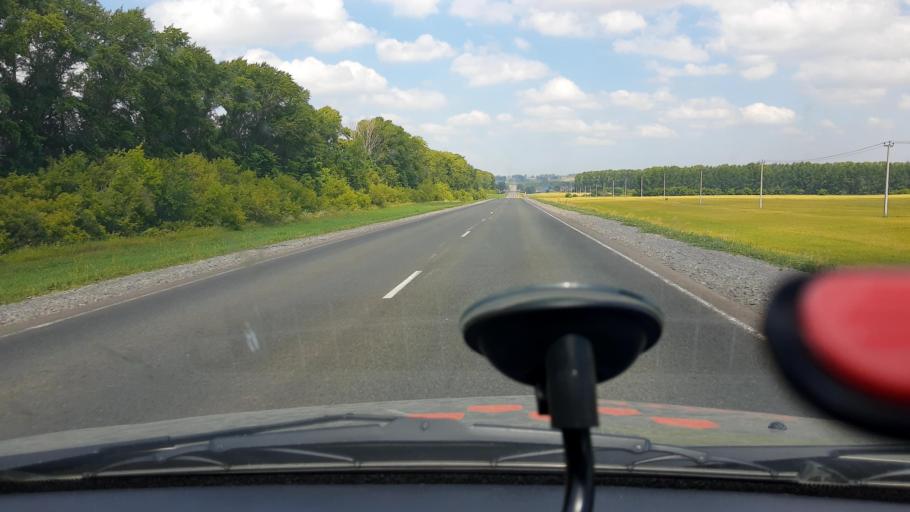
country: RU
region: Bashkortostan
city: Buzdyak
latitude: 54.6698
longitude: 54.5458
